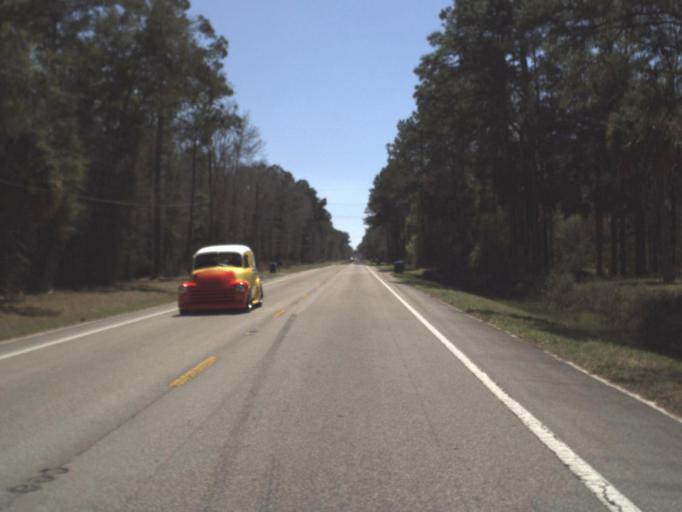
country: US
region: Florida
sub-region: Leon County
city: Woodville
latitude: 30.2012
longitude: -84.2193
